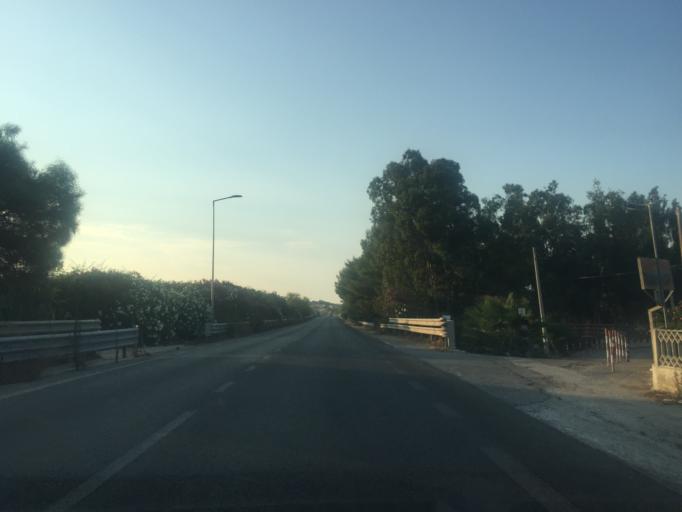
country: IT
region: Sicily
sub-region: Ragusa
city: Cava d'Aliga
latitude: 36.7221
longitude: 14.7511
